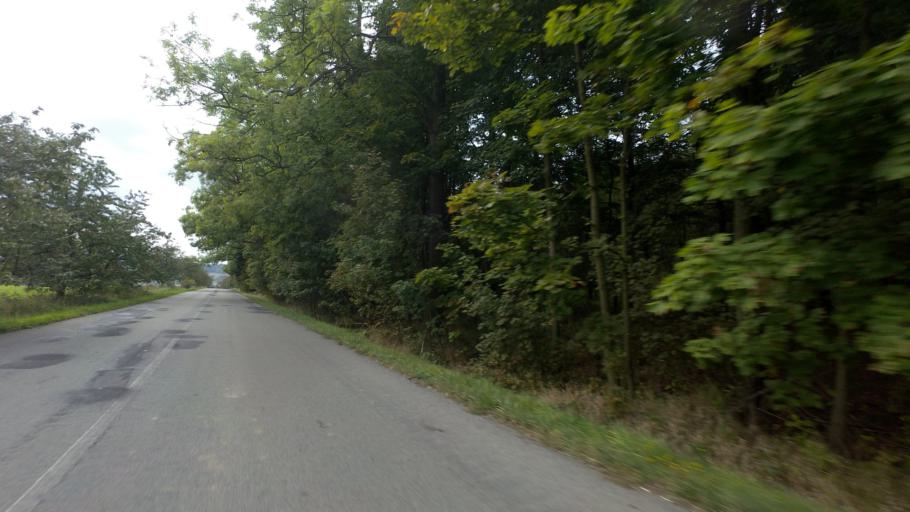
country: CZ
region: Ustecky
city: Velky Senov
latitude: 51.0086
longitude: 14.3742
